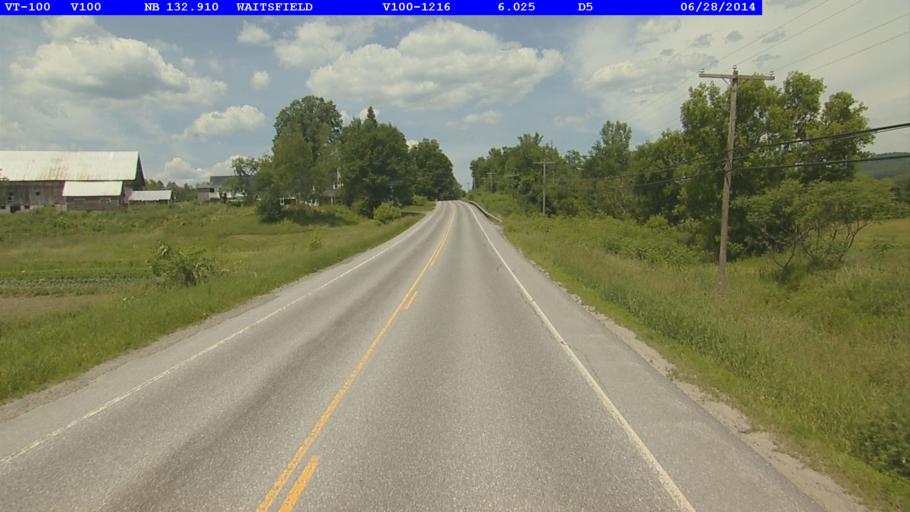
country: US
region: Vermont
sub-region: Washington County
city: Waterbury
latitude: 44.2149
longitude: -72.7927
